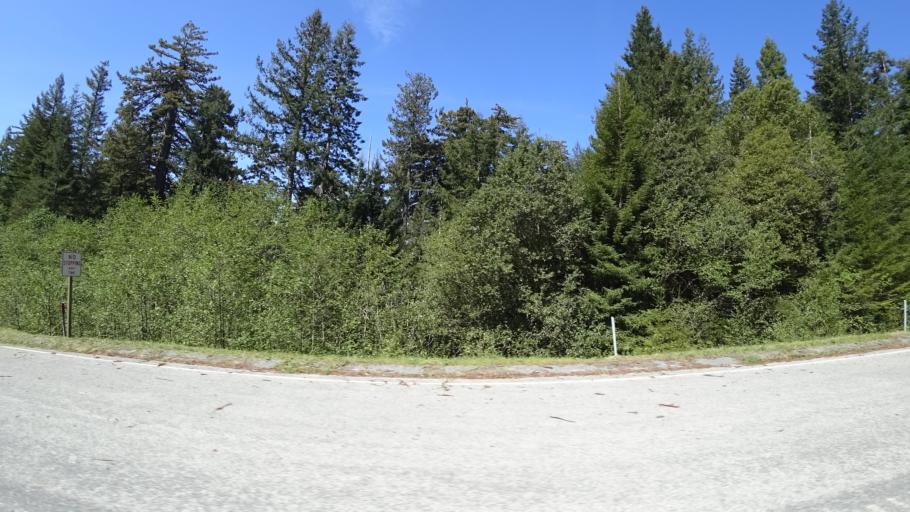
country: US
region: California
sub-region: Humboldt County
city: Westhaven-Moonstone
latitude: 41.3802
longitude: -123.9951
